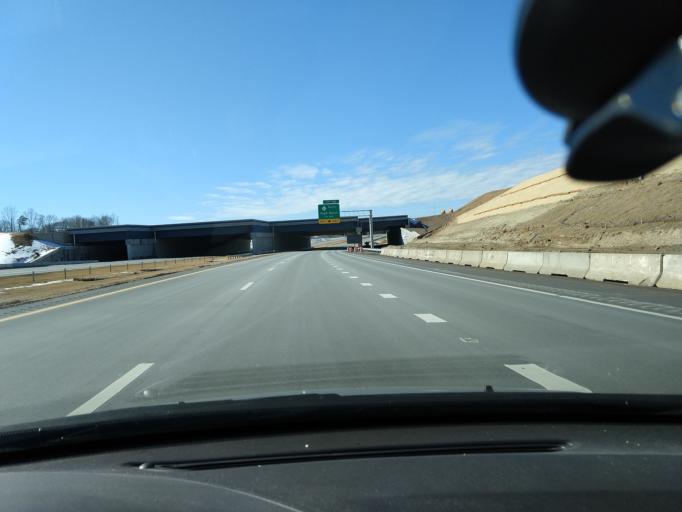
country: US
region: North Carolina
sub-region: Guilford County
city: Oak Ridge
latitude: 36.1206
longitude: -79.9451
